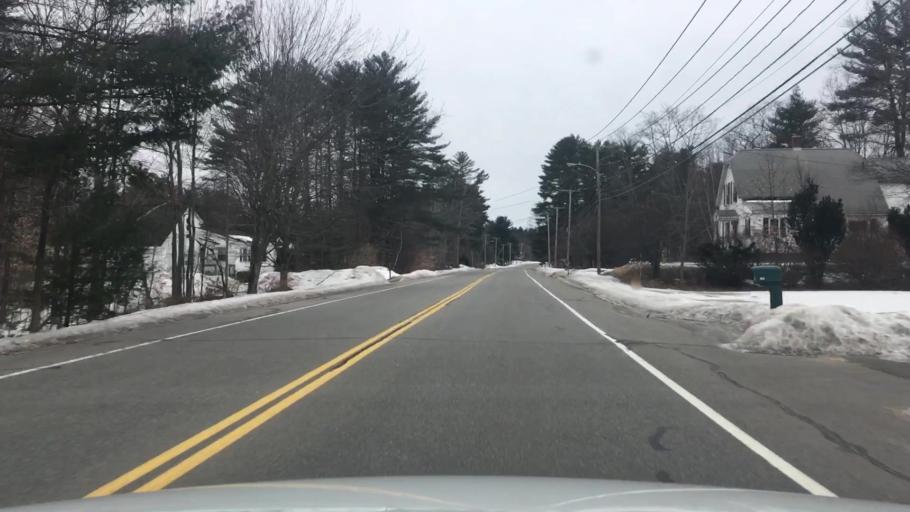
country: US
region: Maine
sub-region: York County
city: Springvale
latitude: 43.4786
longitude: -70.8165
